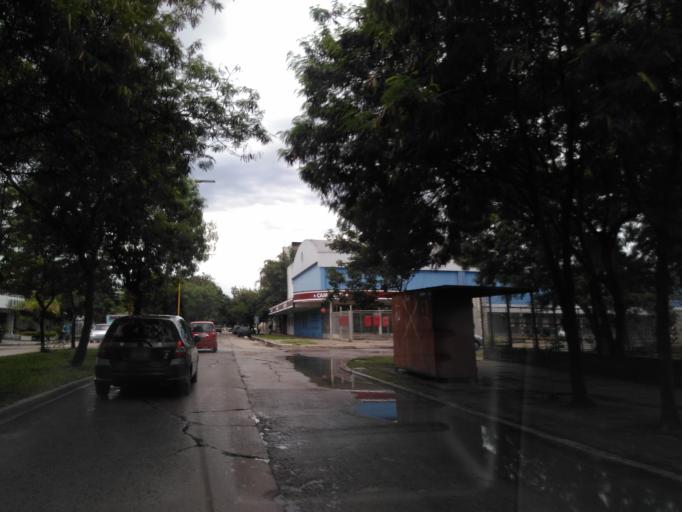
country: AR
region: Chaco
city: Resistencia
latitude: -27.4586
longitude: -58.9947
